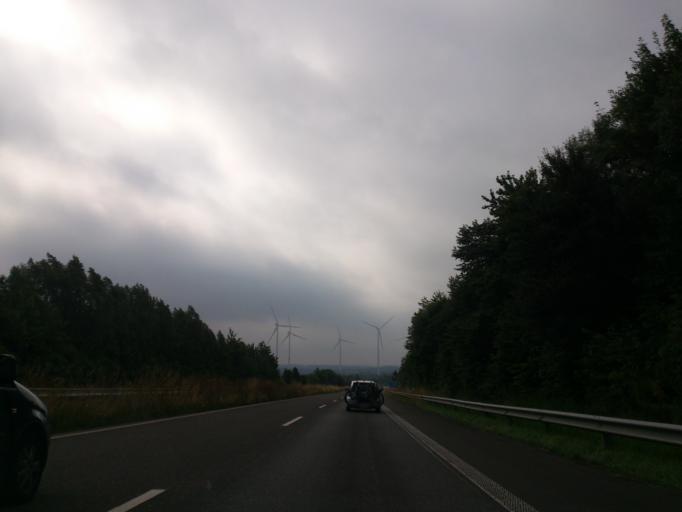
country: DE
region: Schleswig-Holstein
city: Arkebek
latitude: 54.1514
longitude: 9.2373
